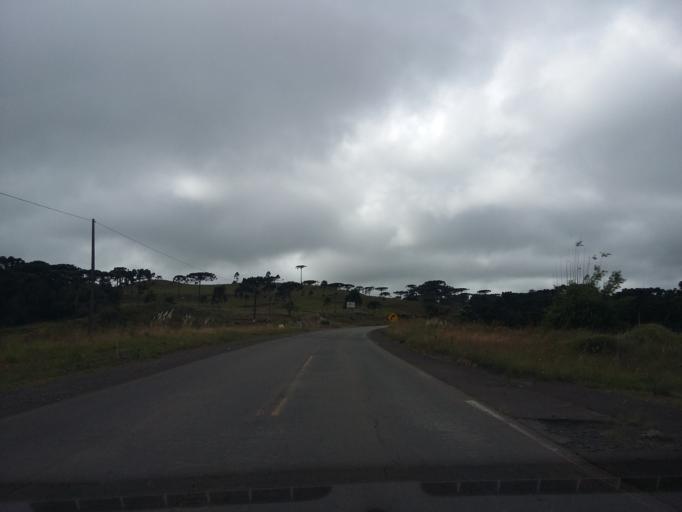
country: BR
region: Santa Catarina
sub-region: Lages
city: Lages
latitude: -27.8943
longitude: -50.1327
